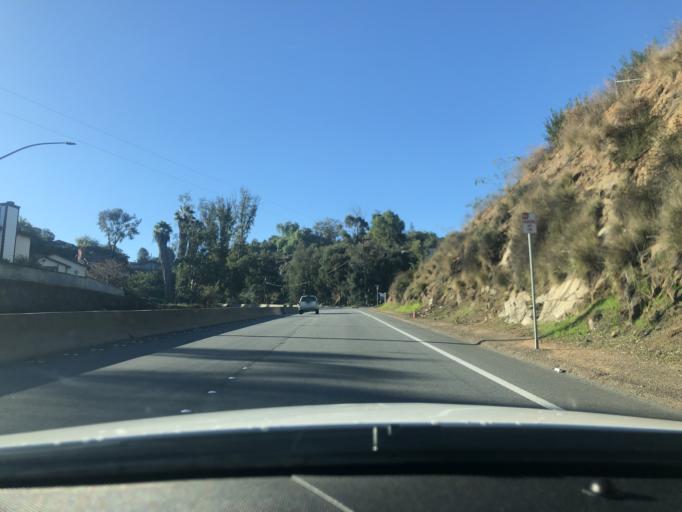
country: US
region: California
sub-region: San Diego County
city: Casa de Oro-Mount Helix
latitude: 32.7764
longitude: -116.9585
